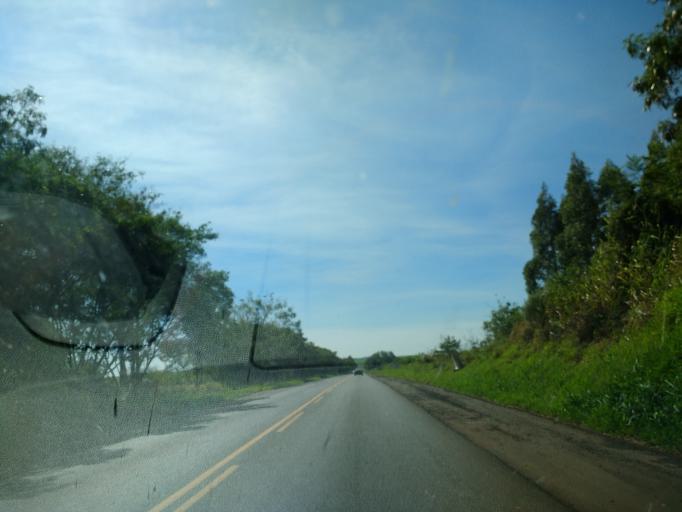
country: BR
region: Parana
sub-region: Umuarama
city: Umuarama
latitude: -23.8632
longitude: -53.3866
